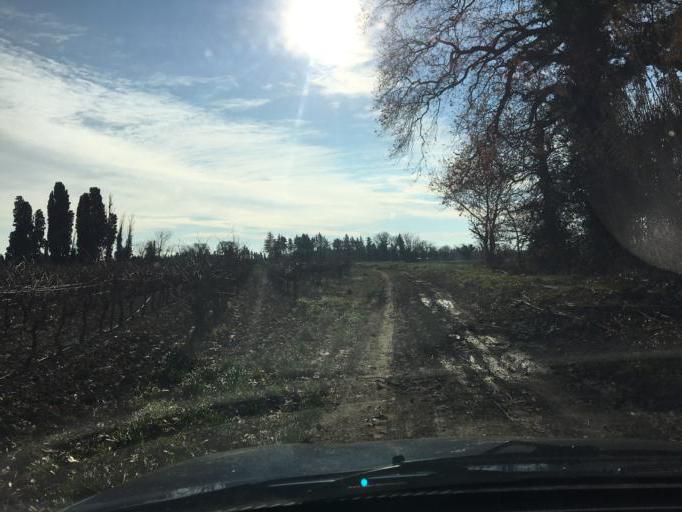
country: FR
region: Provence-Alpes-Cote d'Azur
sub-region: Departement du Vaucluse
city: Jonquieres
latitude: 44.1432
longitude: 4.8989
